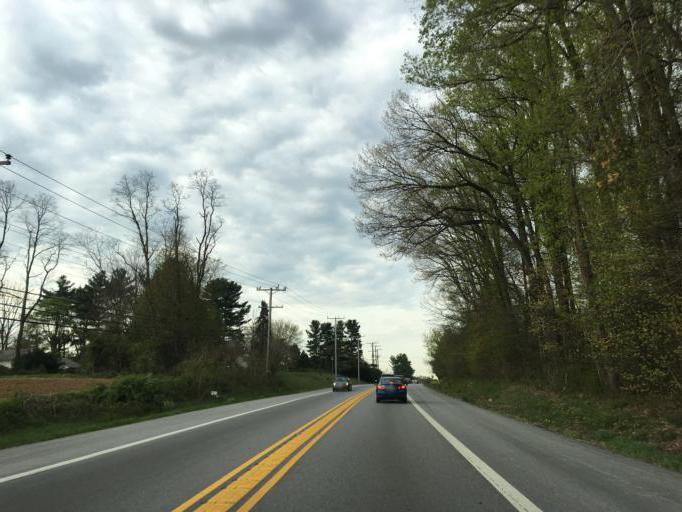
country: US
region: Maryland
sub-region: Carroll County
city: Sykesville
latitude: 39.3256
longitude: -76.9484
